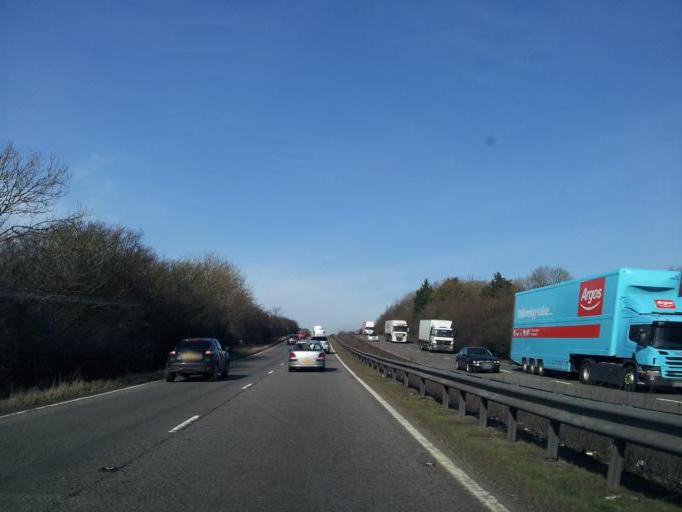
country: GB
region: England
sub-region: District of Rutland
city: Clipsham
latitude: 52.7920
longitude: -0.6106
